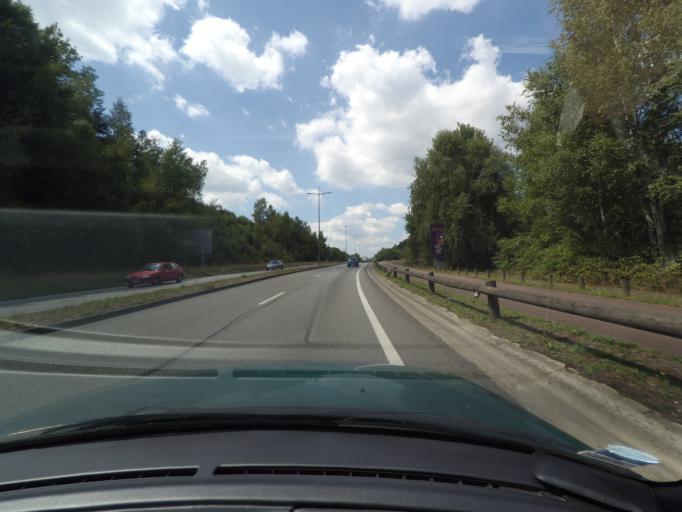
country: FR
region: Limousin
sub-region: Departement de la Haute-Vienne
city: Condat-sur-Vienne
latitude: 45.8034
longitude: 1.2898
